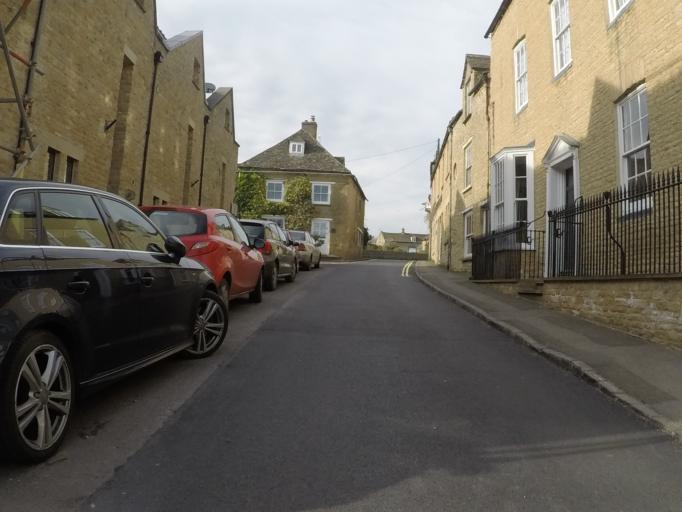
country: GB
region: England
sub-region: Oxfordshire
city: Charlbury
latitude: 51.8714
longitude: -1.4840
